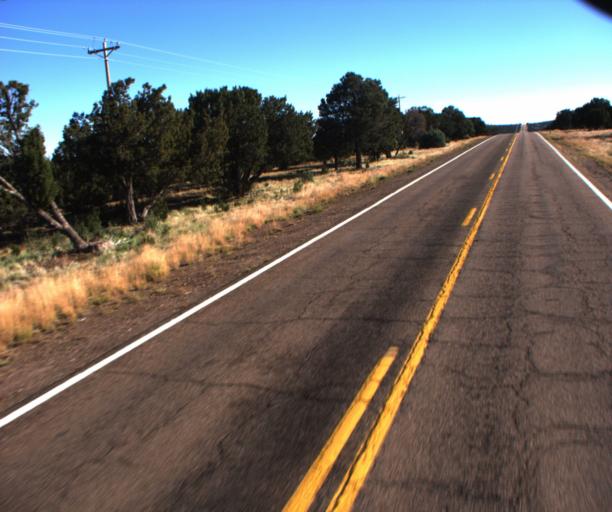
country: US
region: Arizona
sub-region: Navajo County
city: White Mountain Lake
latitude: 34.2945
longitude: -109.8014
